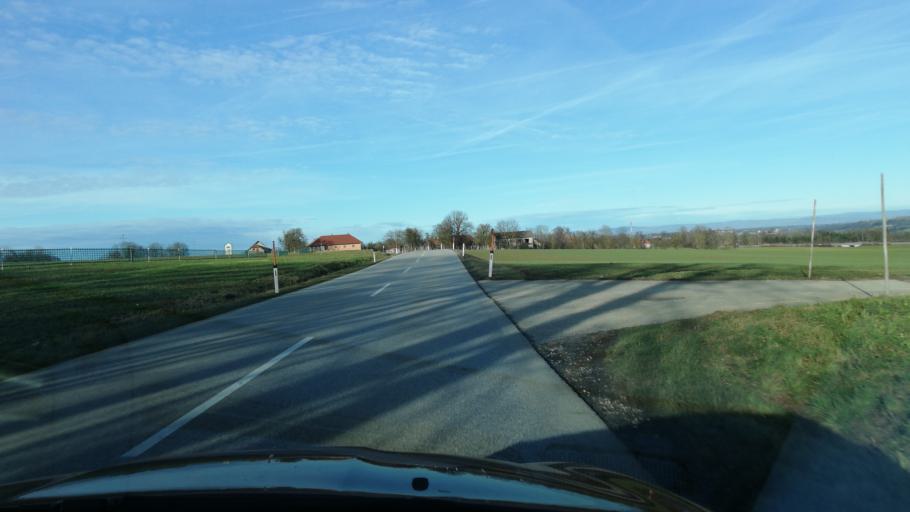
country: AT
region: Upper Austria
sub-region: Politischer Bezirk Kirchdorf an der Krems
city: Kremsmunster
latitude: 47.9875
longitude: 14.0794
